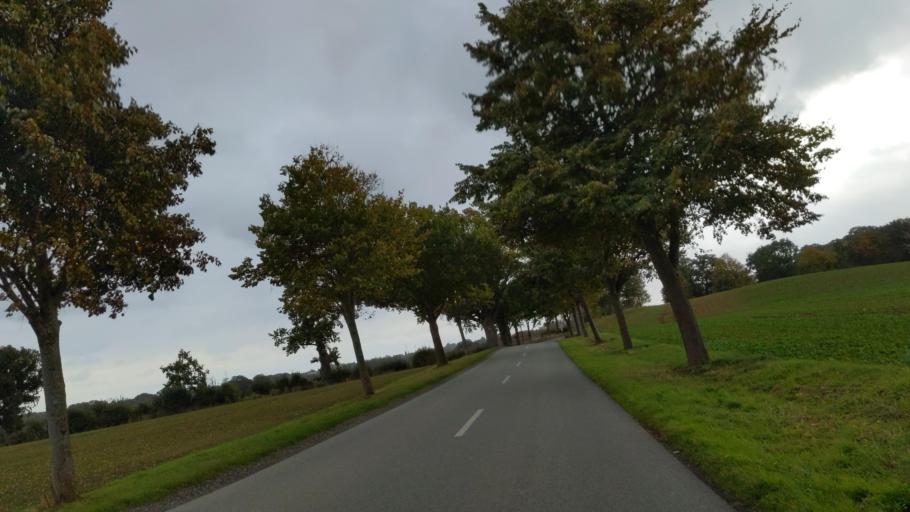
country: DE
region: Schleswig-Holstein
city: Neustadt in Holstein
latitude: 54.1209
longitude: 10.7796
